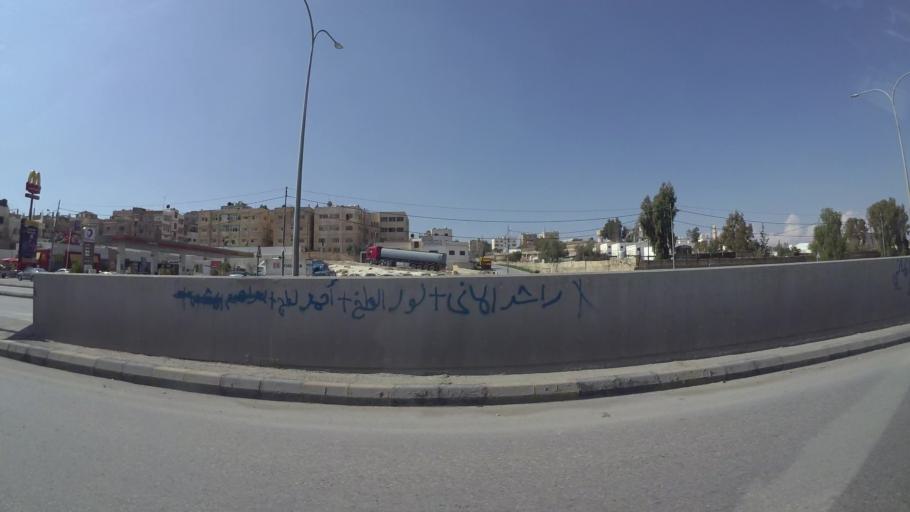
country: JO
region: Zarqa
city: Zarqa
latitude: 32.0794
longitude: 36.1051
